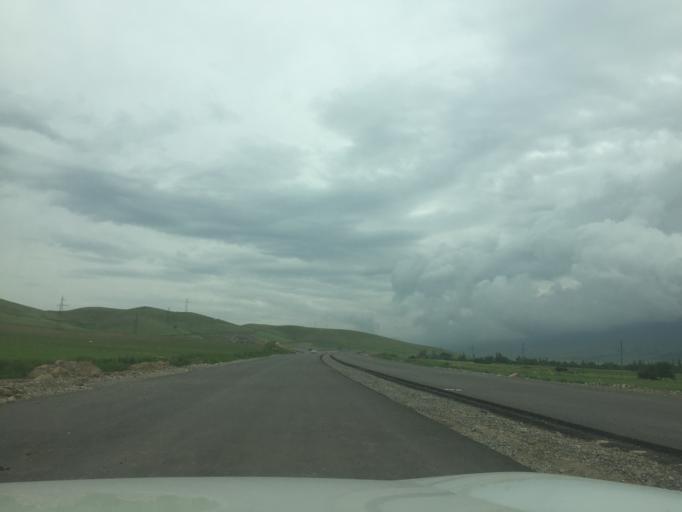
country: KZ
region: Ongtustik Qazaqstan
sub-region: Tulkibas Audany
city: Zhabagly
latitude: 42.5176
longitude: 70.5518
